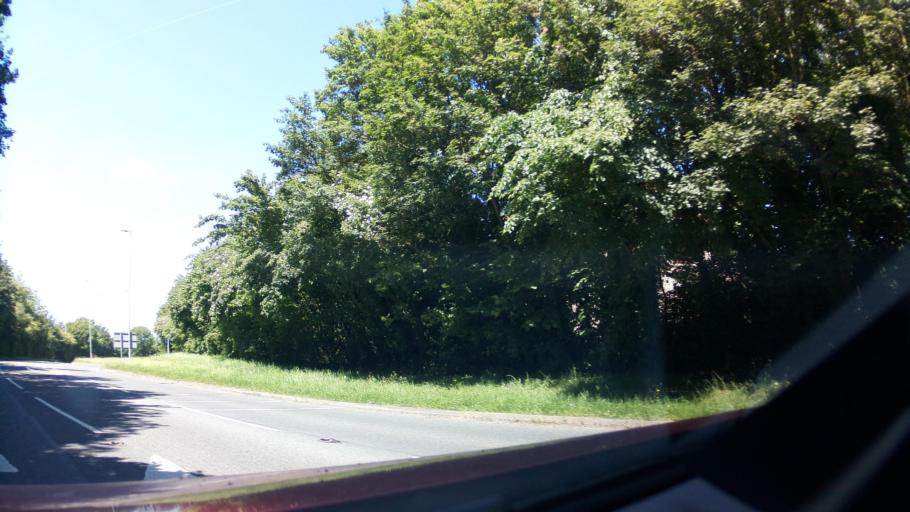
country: GB
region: England
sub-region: Wiltshire
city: Calne
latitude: 51.4408
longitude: -2.0182
